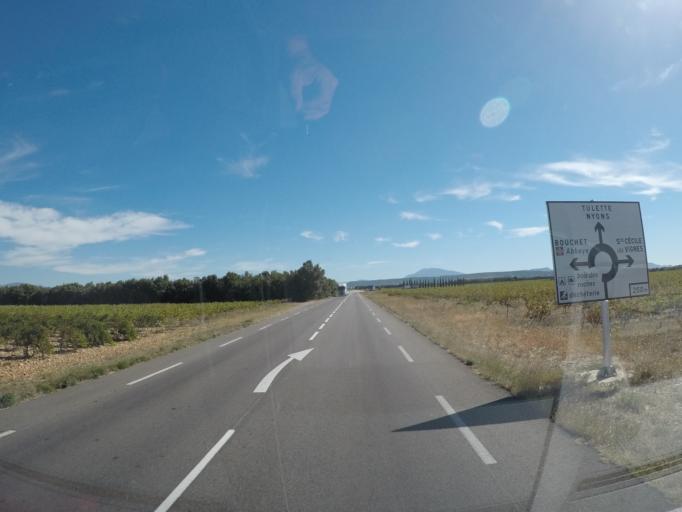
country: FR
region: Rhone-Alpes
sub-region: Departement de la Drome
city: Suze-la-Rousse
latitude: 44.2859
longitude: 4.8697
